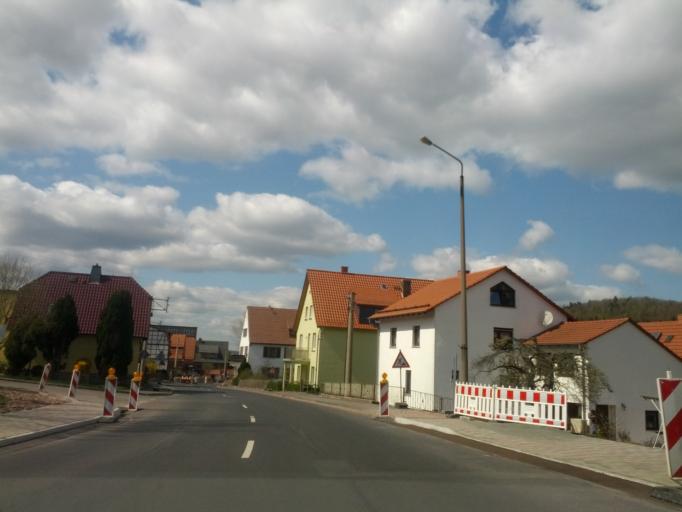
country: DE
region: Thuringia
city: Seebach
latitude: 50.9125
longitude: 10.4246
